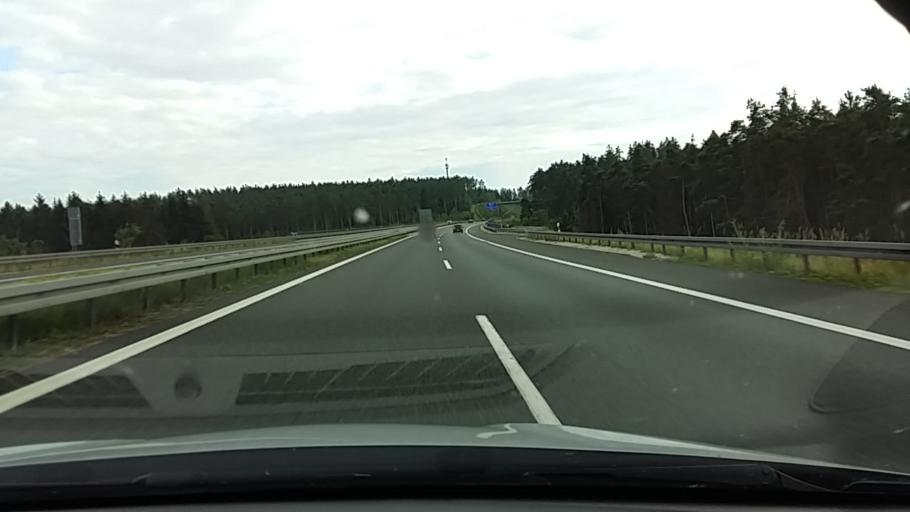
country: DE
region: Bavaria
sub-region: Upper Palatinate
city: Wernberg-Koblitz
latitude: 49.5343
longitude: 12.1906
